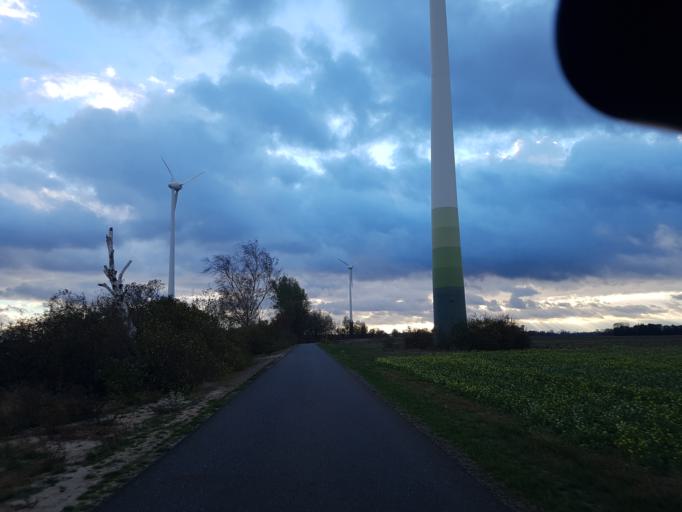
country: DE
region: Saxony-Anhalt
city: Elster
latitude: 51.8300
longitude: 12.8715
